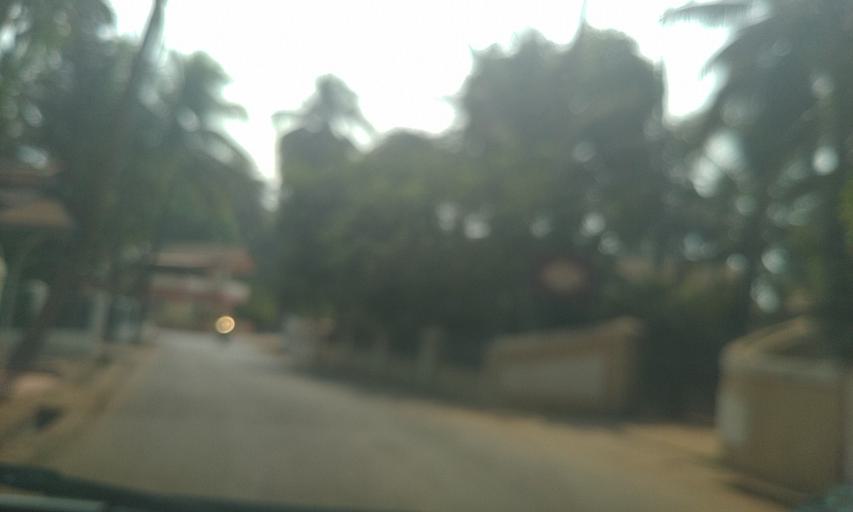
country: IN
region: Goa
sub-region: North Goa
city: Taleigao
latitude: 15.4673
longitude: 73.8206
